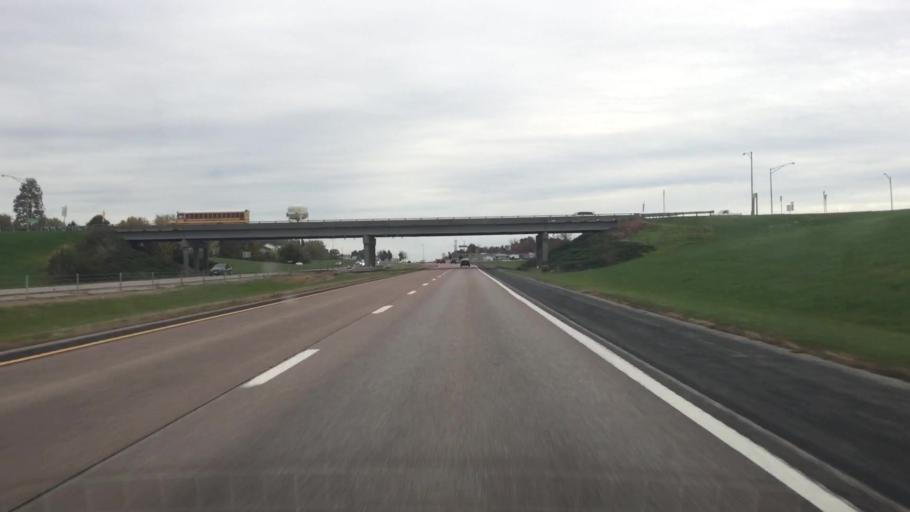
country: US
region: Missouri
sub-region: Boone County
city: Ashland
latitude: 38.7732
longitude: -92.2521
